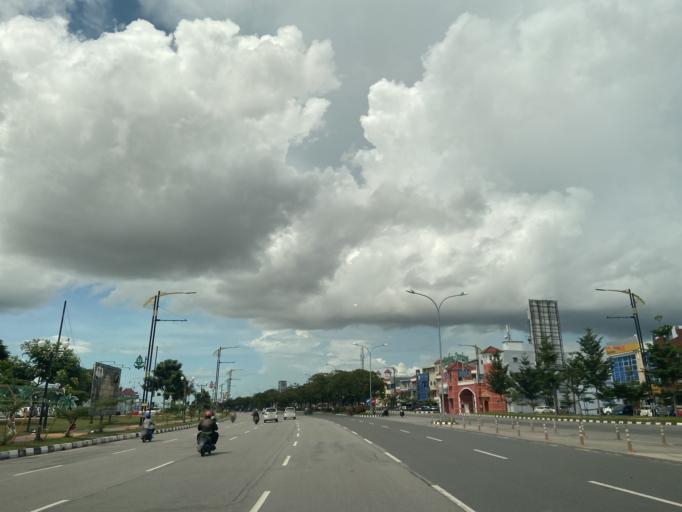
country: SG
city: Singapore
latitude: 1.1249
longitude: 104.0271
